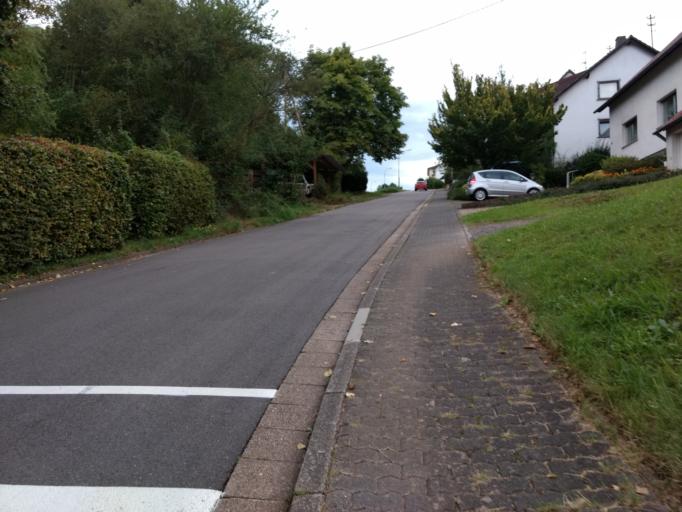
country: DE
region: Saarland
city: Schmelz
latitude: 49.3876
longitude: 6.8418
